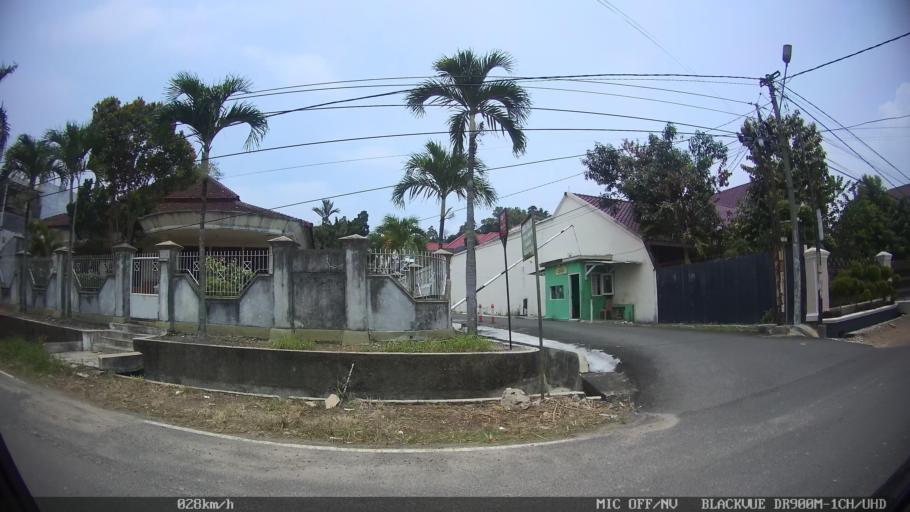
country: ID
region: Lampung
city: Bandarlampung
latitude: -5.4142
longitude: 105.2694
